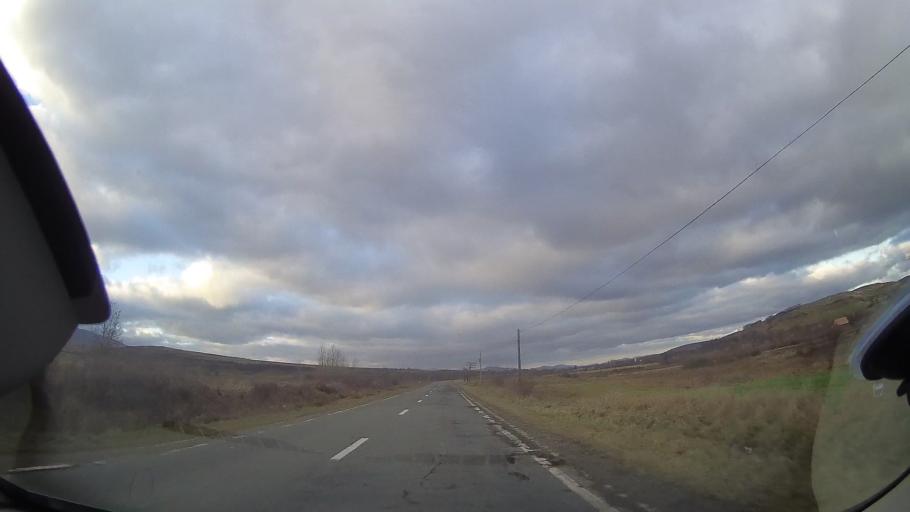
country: RO
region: Cluj
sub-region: Comuna Calatele
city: Calatele
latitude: 46.7896
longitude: 22.9985
